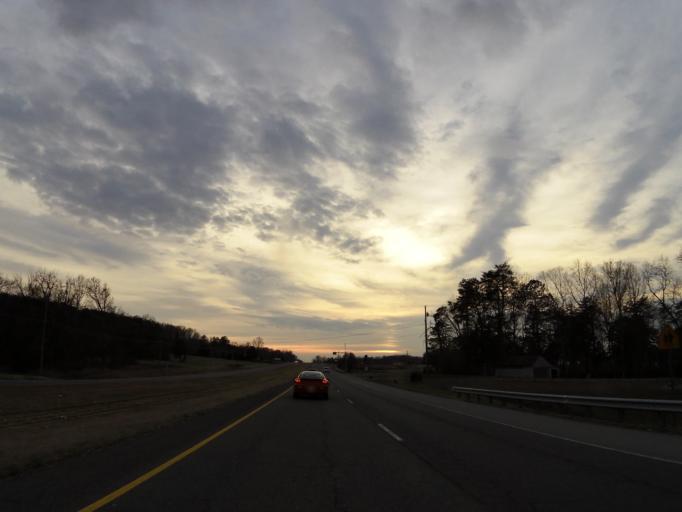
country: US
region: Tennessee
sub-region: Monroe County
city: Madisonville
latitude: 35.5499
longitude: -84.3150
